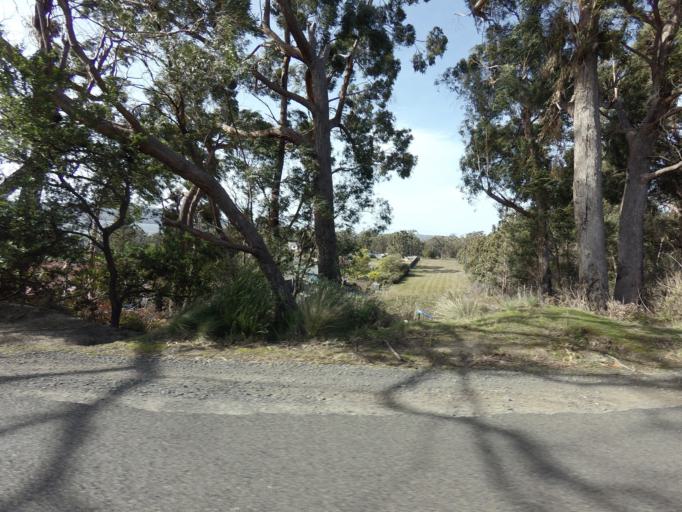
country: AU
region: Tasmania
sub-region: Kingborough
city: Margate
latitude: -43.0764
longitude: 147.2654
